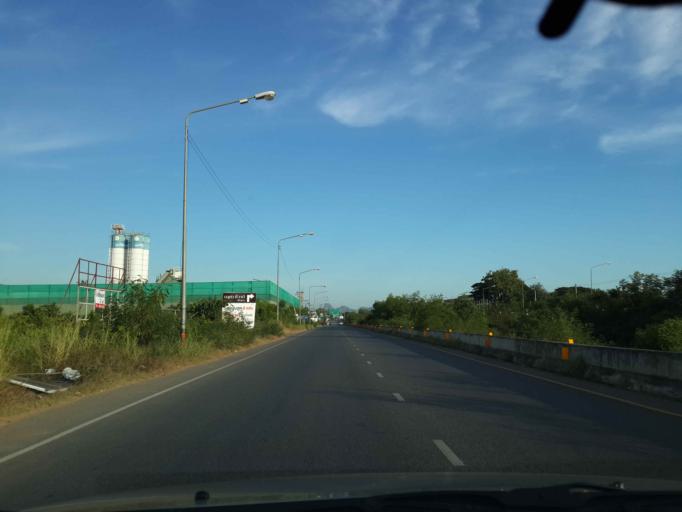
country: TH
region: Chon Buri
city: Phatthaya
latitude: 12.8625
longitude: 100.9129
